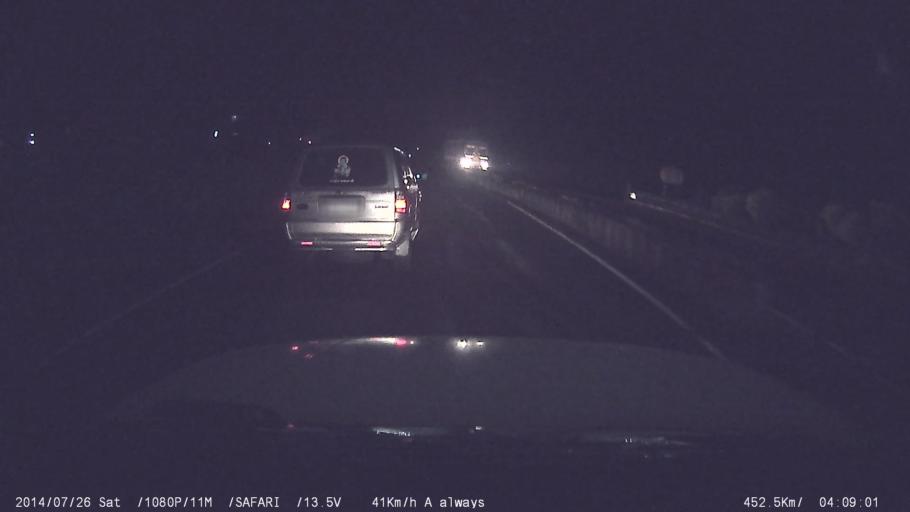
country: IN
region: Kerala
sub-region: Thrissur District
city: Trichur
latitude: 10.5309
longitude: 76.2594
